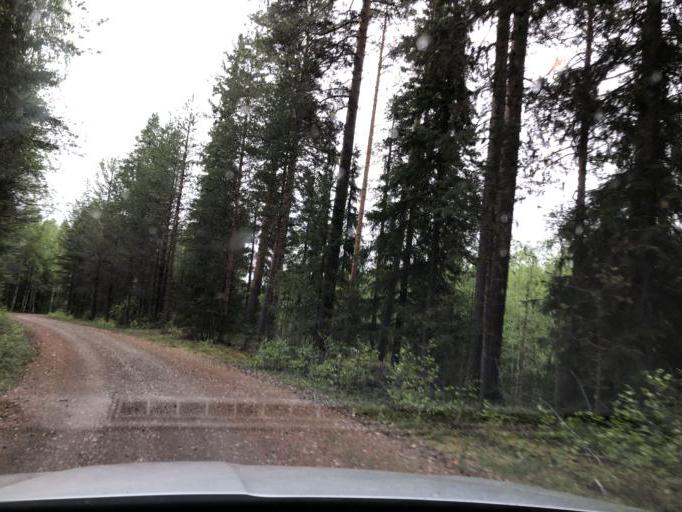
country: SE
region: Norrbotten
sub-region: Pitea Kommun
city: Roknas
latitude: 65.3952
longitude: 21.2663
